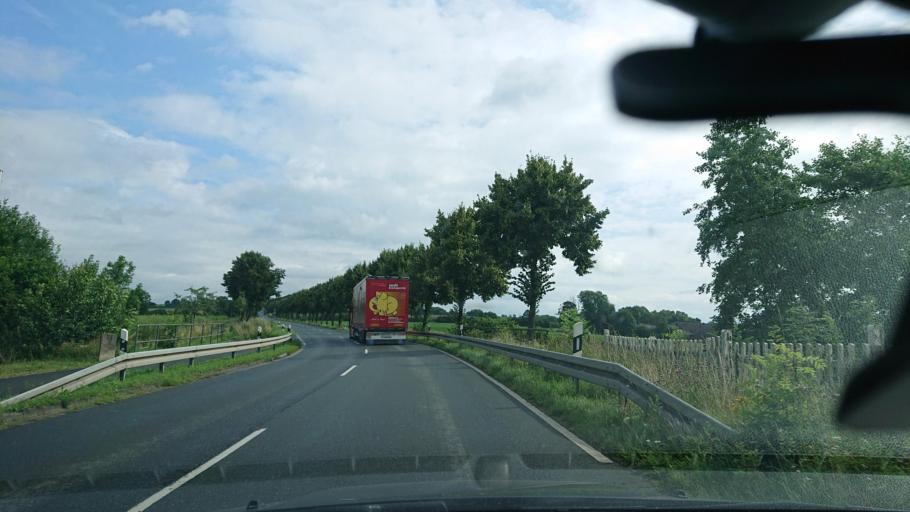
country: DE
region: North Rhine-Westphalia
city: Lunen
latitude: 51.6299
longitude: 7.5623
